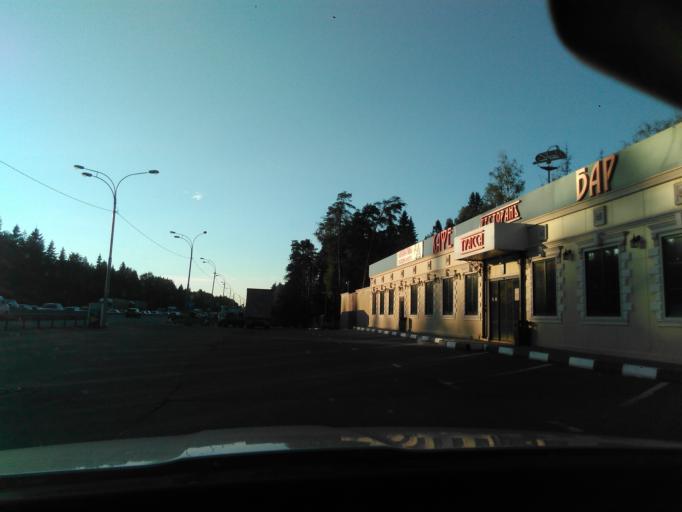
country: RU
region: Moskovskaya
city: Lozhki
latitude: 56.0786
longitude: 37.1252
